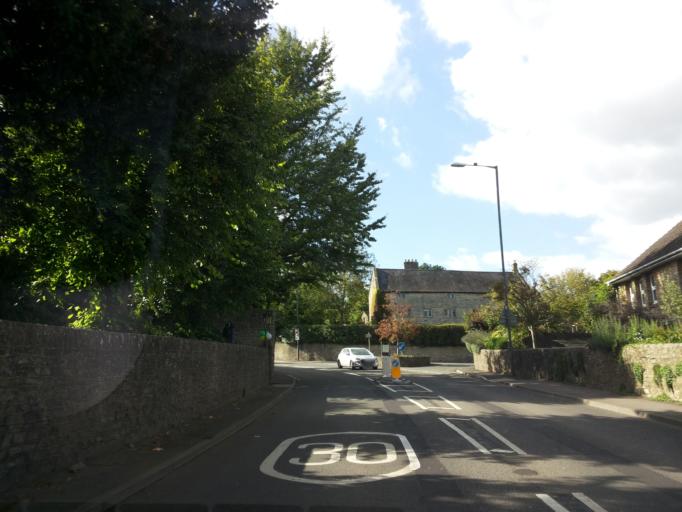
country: GB
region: England
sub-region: Bath and North East Somerset
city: Corston
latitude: 51.3861
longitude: -2.4397
